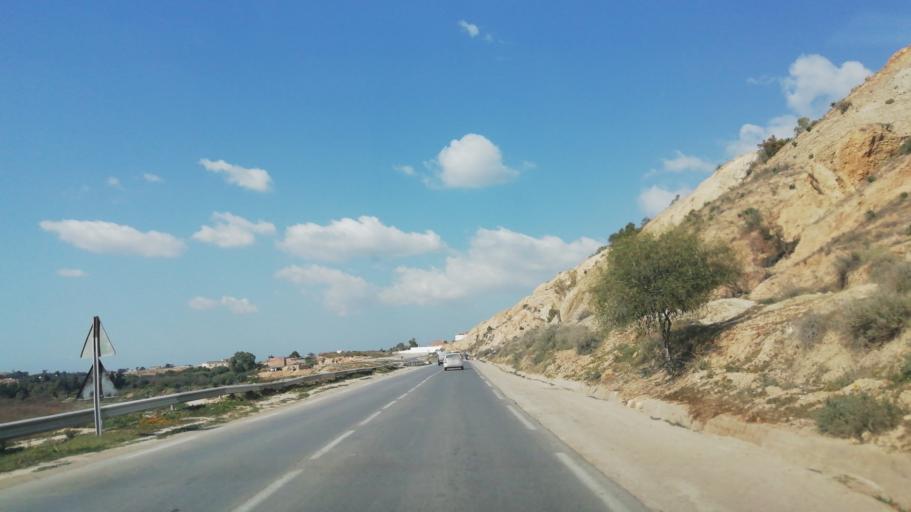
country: DZ
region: Mascara
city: Mascara
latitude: 35.5679
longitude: 0.0711
